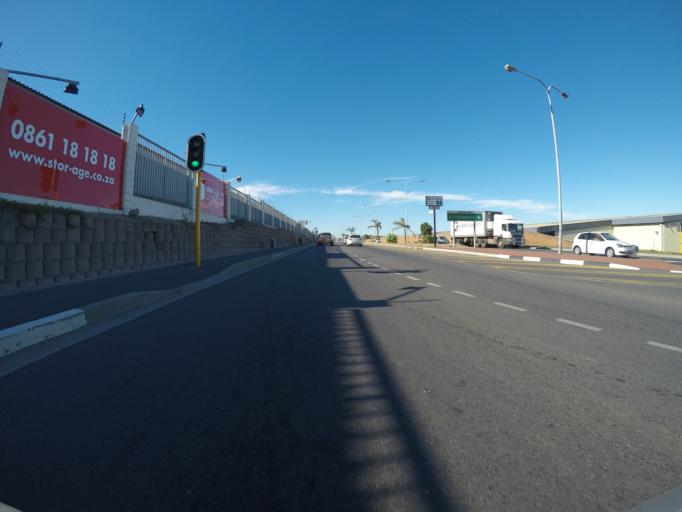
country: ZA
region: Western Cape
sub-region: City of Cape Town
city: Kraaifontein
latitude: -33.9060
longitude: 18.6673
